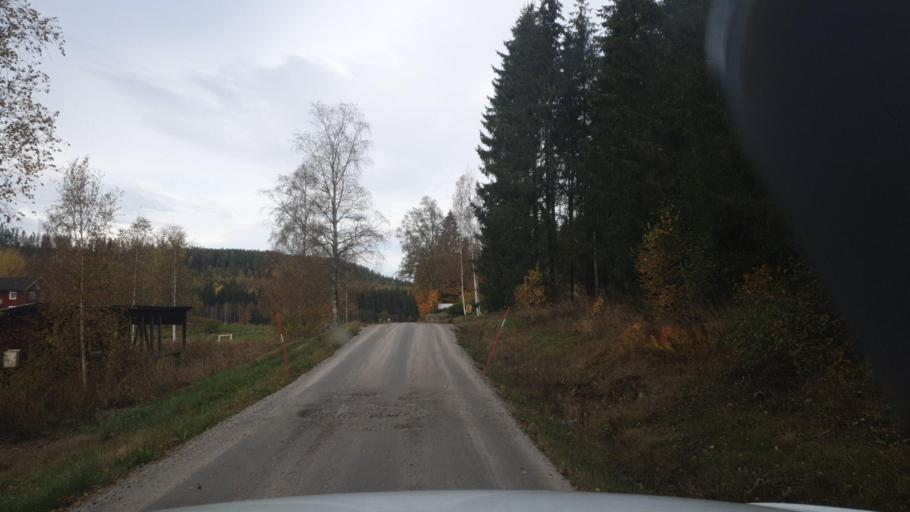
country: SE
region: Vaermland
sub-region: Sunne Kommun
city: Sunne
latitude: 59.7079
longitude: 12.8783
